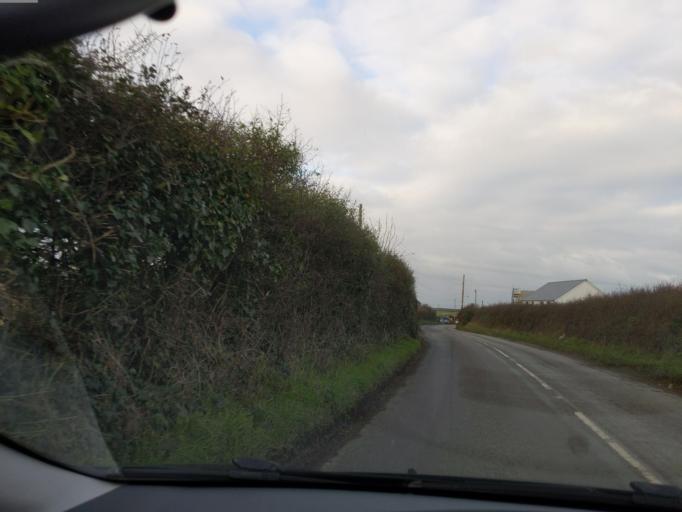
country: GB
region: England
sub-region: Cornwall
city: Padstow
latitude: 50.5343
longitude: -4.9512
